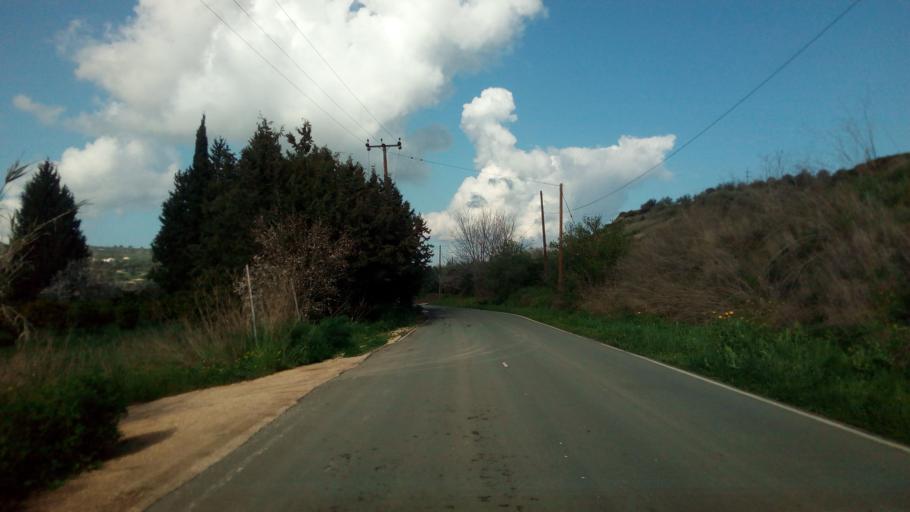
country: CY
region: Pafos
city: Polis
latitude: 34.9801
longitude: 32.4611
